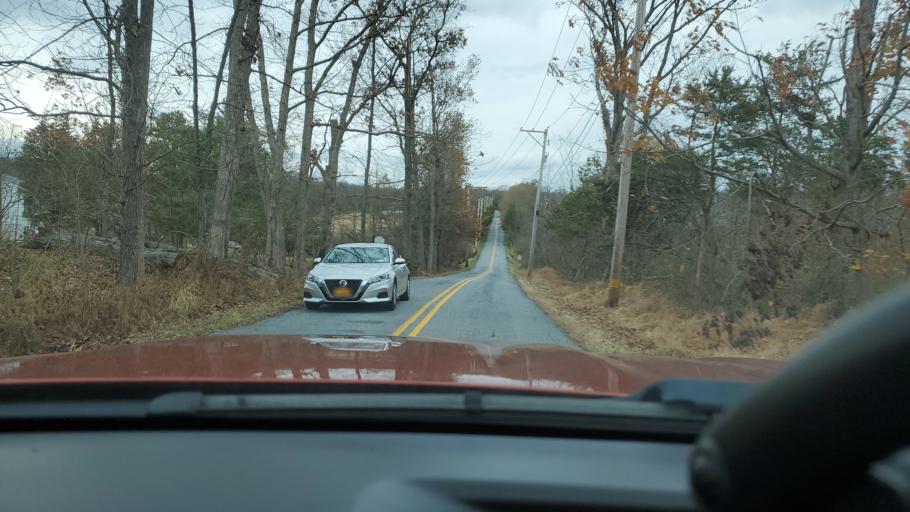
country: US
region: Pennsylvania
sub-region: Montgomery County
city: Spring Mount
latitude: 40.3009
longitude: -75.4978
